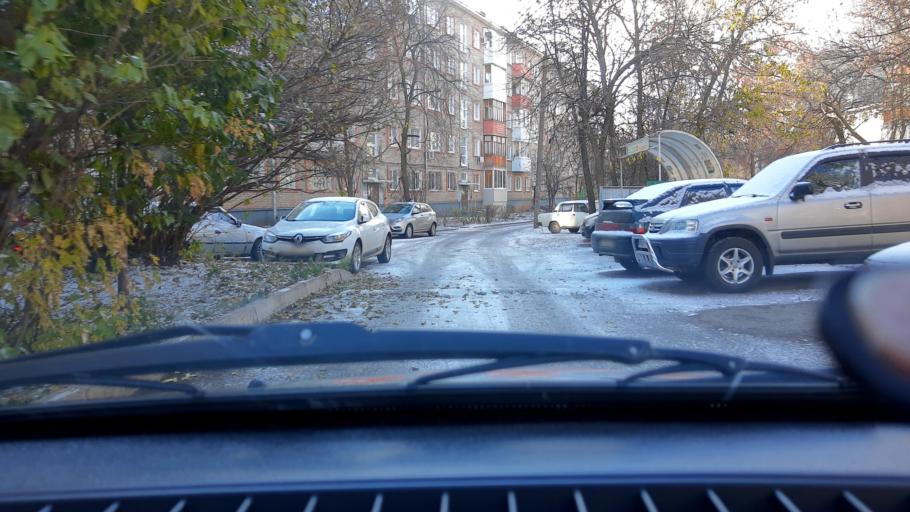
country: RU
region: Bashkortostan
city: Ufa
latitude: 54.7768
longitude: 56.0228
